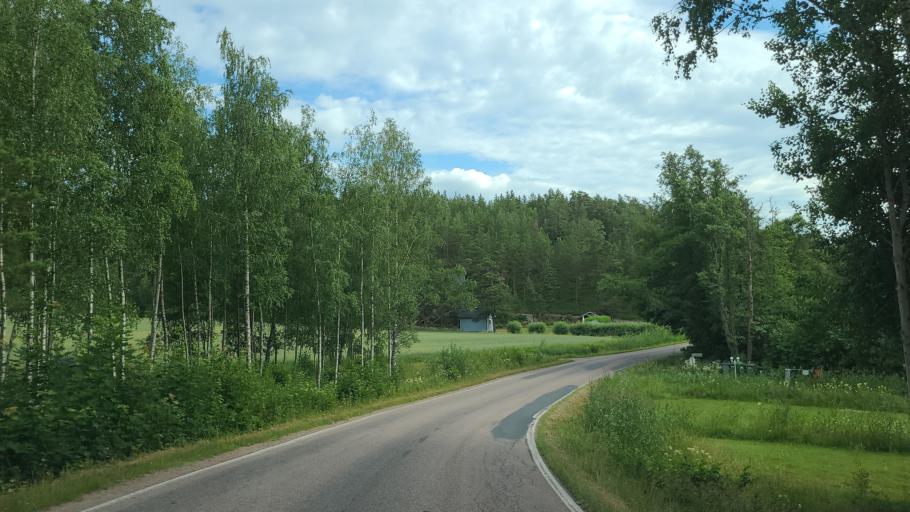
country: FI
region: Varsinais-Suomi
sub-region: Turku
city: Rymaettylae
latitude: 60.3445
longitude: 21.9781
